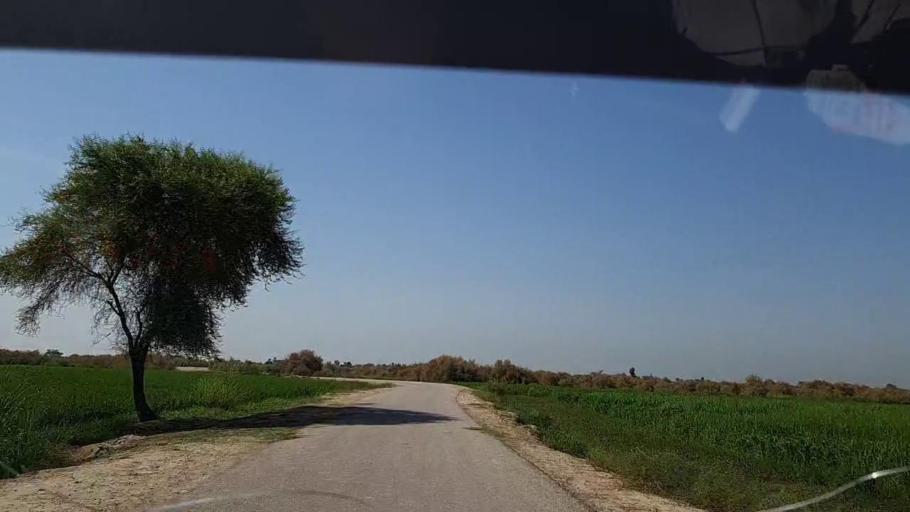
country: PK
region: Sindh
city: Kandhkot
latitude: 28.3127
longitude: 69.1001
